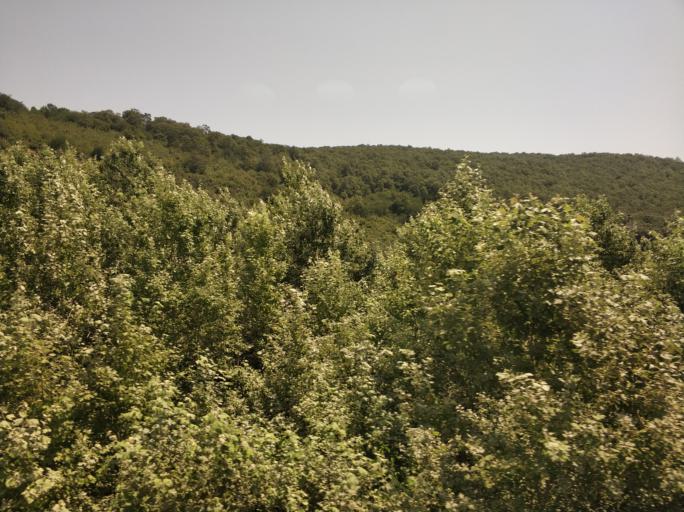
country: IR
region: Gilan
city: Pa'in-e Bazar-e Rudbar
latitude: 36.9481
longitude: 49.5485
